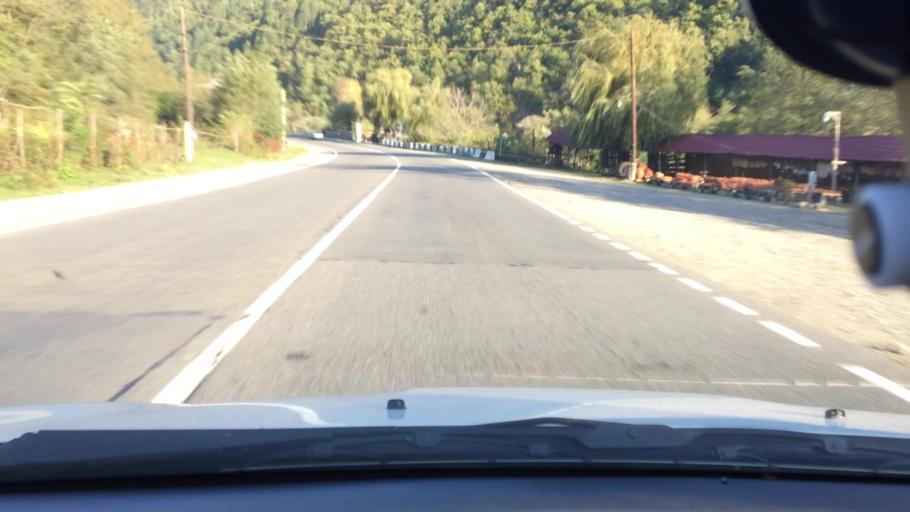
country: GE
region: Imereti
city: Kharagauli
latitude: 42.1066
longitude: 43.3398
